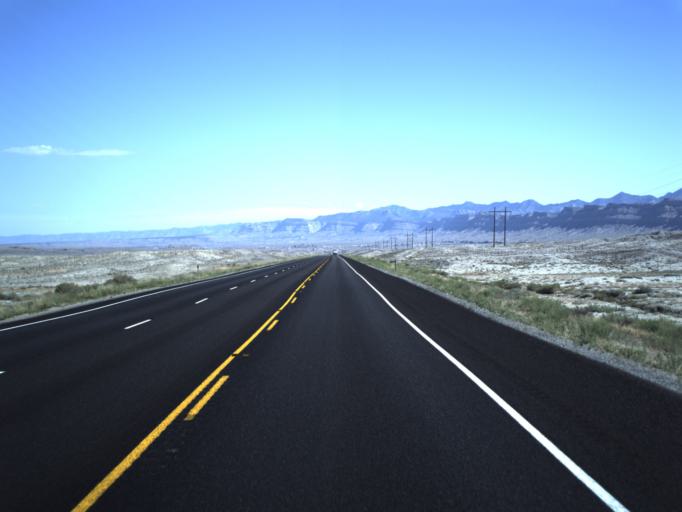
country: US
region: Utah
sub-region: Carbon County
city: East Carbon City
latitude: 39.2035
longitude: -110.3385
